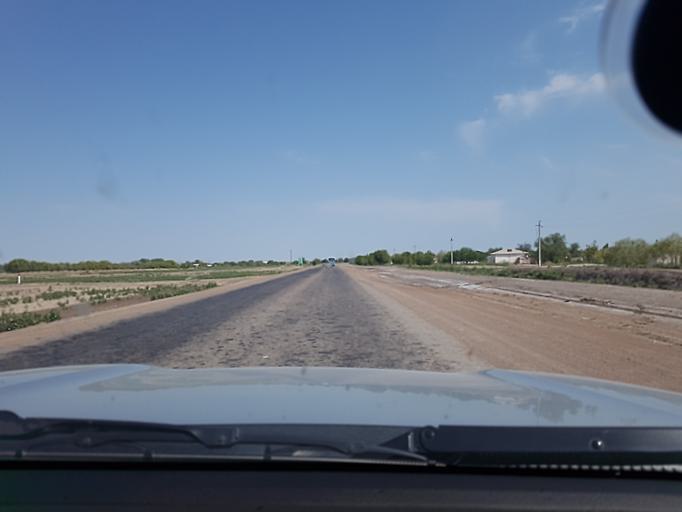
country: TM
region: Dasoguz
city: Boldumsaz
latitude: 42.1584
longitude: 59.6050
